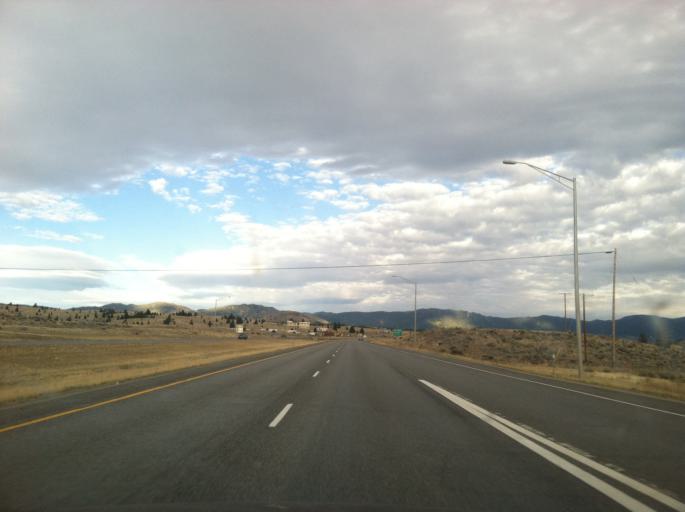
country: US
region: Montana
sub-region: Silver Bow County
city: Butte
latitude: 46.0084
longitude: -112.6337
